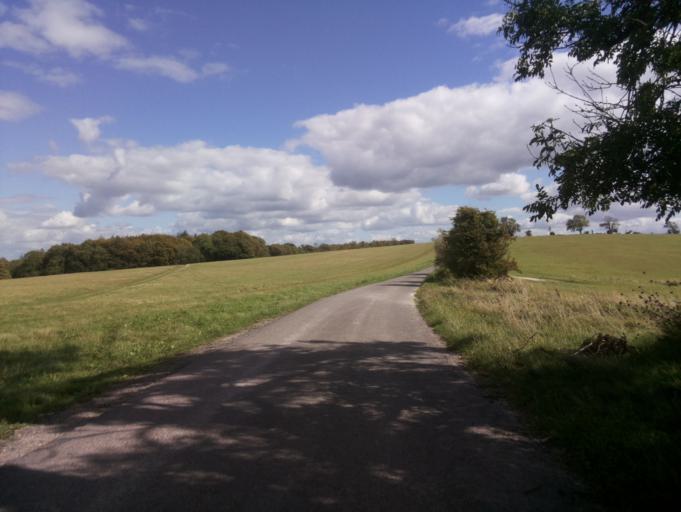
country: GB
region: England
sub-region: Wiltshire
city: Erlestoke
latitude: 51.2757
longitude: -2.0725
